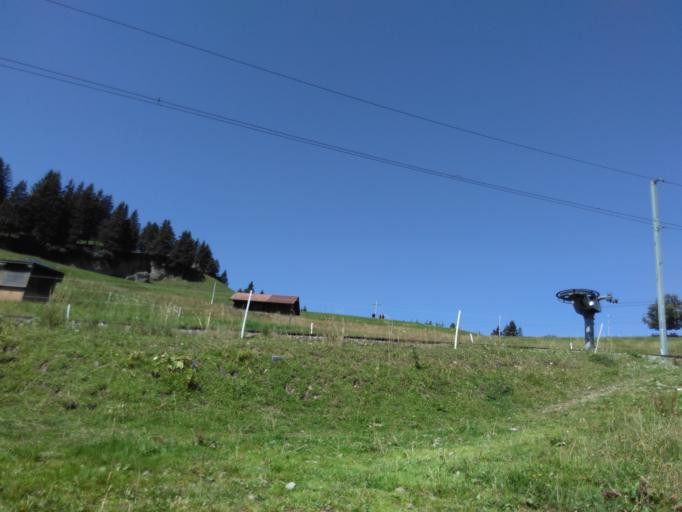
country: CH
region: Lucerne
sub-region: Lucerne-Land District
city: Vitznau
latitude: 47.0500
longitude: 8.4724
